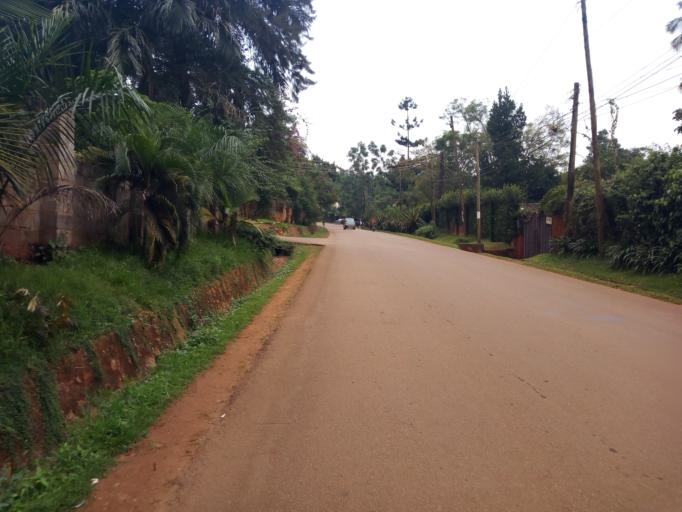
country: UG
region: Central Region
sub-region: Wakiso District
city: Kireka
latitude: 0.3258
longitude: 32.6248
